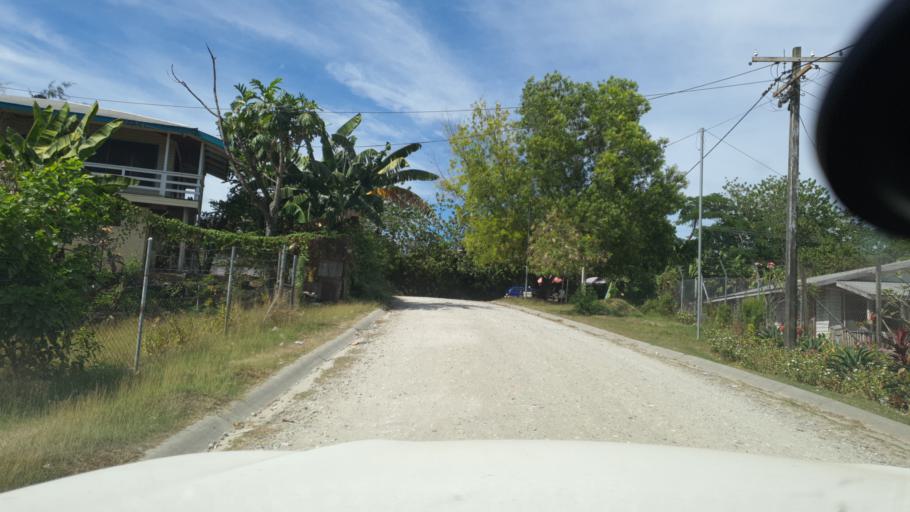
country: SB
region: Guadalcanal
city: Honiara
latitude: -9.4422
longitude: 159.9734
